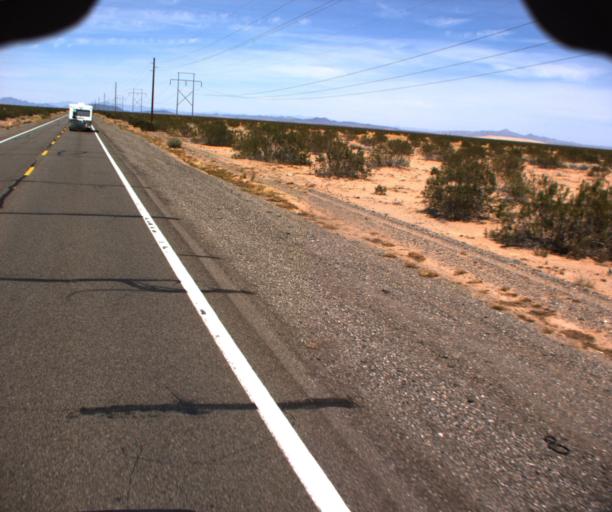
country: US
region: Arizona
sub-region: La Paz County
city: Parker
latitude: 33.9186
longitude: -114.2169
